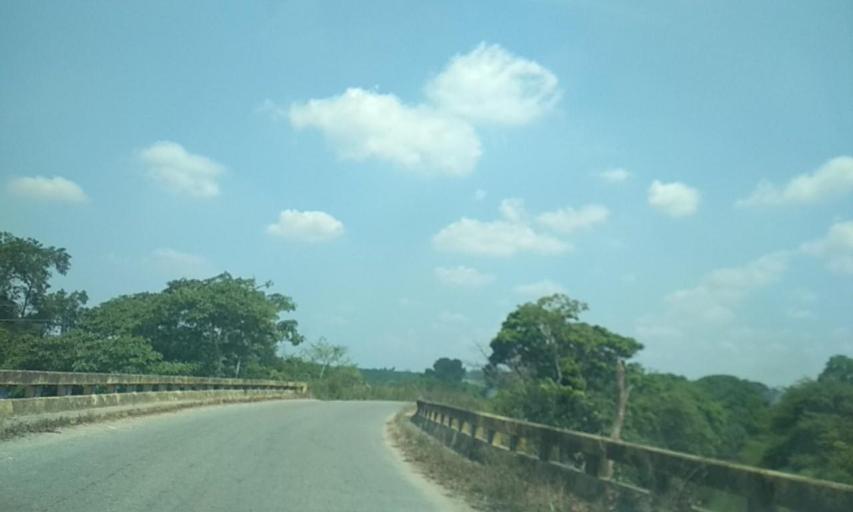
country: MX
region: Tabasco
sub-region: Cardenas
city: Poblado C-33 20 de Noviembre
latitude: 17.8492
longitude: -93.6077
